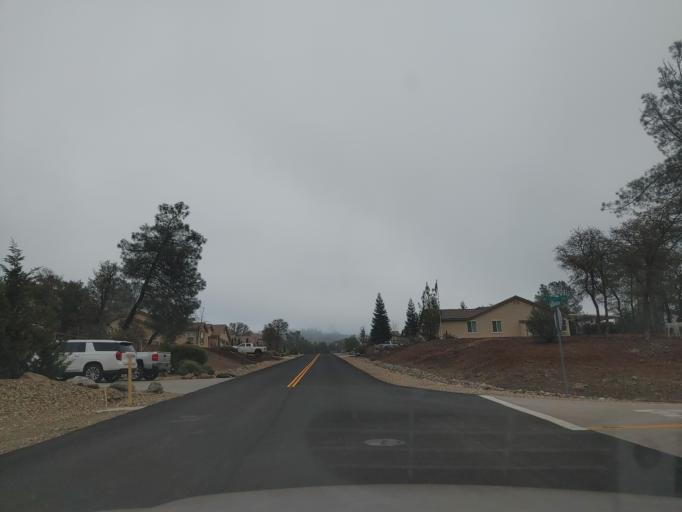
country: US
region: California
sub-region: Calaveras County
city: Copperopolis
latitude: 37.9348
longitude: -120.6121
